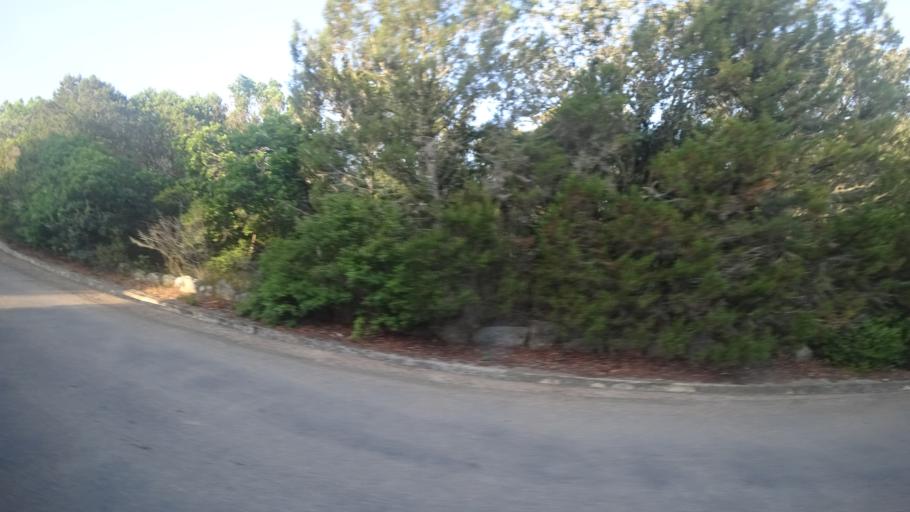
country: FR
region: Corsica
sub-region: Departement de la Corse-du-Sud
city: Porto-Vecchio
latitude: 41.6197
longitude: 9.3542
